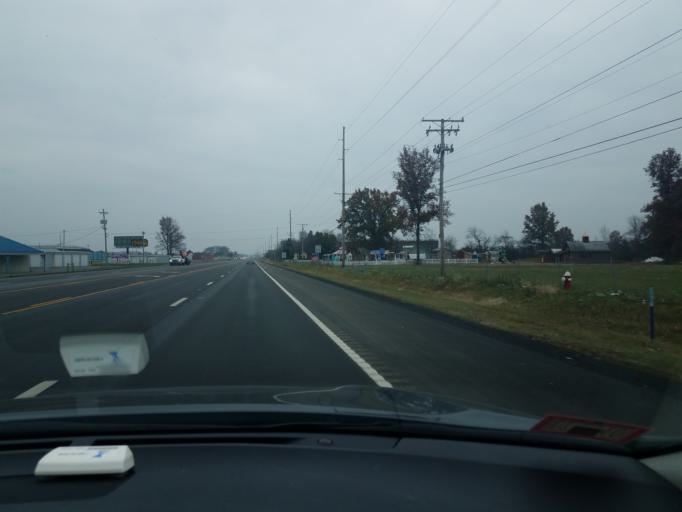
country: US
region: Ohio
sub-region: Erie County
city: Milan
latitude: 41.3779
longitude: -82.6440
